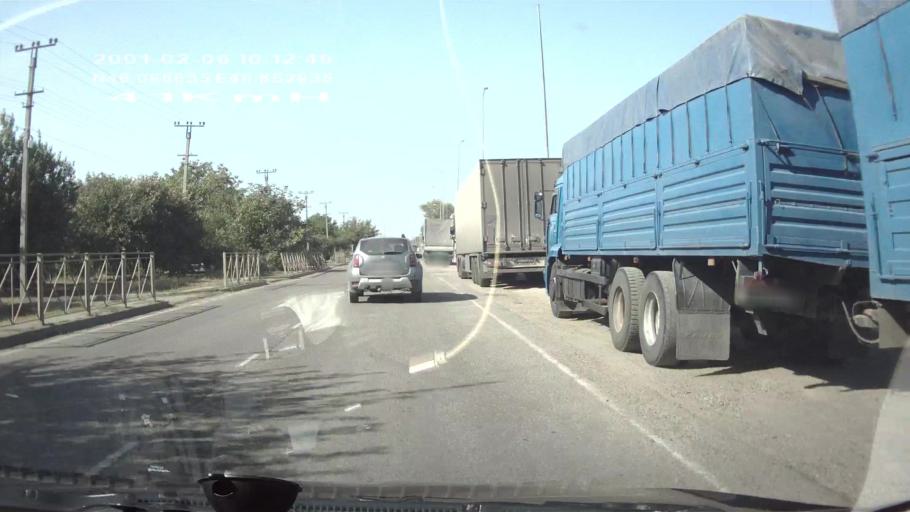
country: RU
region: Krasnodarskiy
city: Belaya Glina
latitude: 46.0966
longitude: 40.8526
